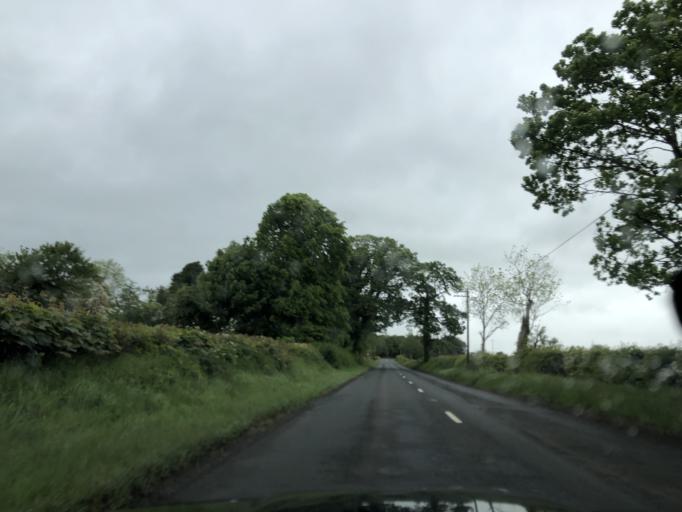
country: GB
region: Northern Ireland
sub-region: Ballymoney District
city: Ballymoney
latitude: 55.1164
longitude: -6.4907
